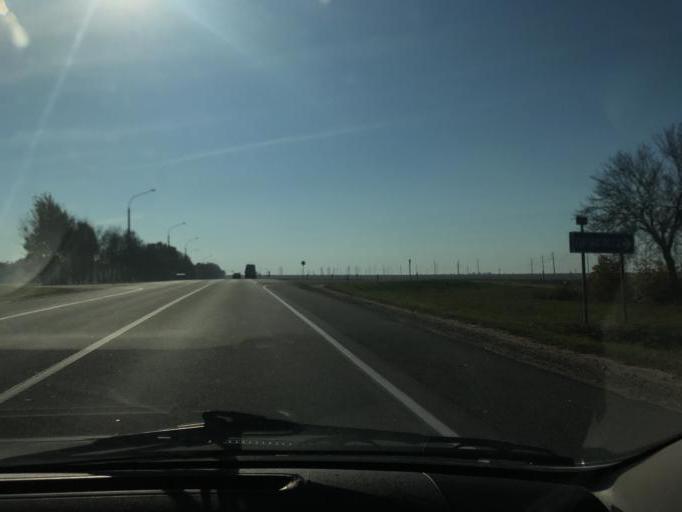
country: BY
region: Minsk
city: Salihorsk
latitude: 52.8743
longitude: 27.4674
